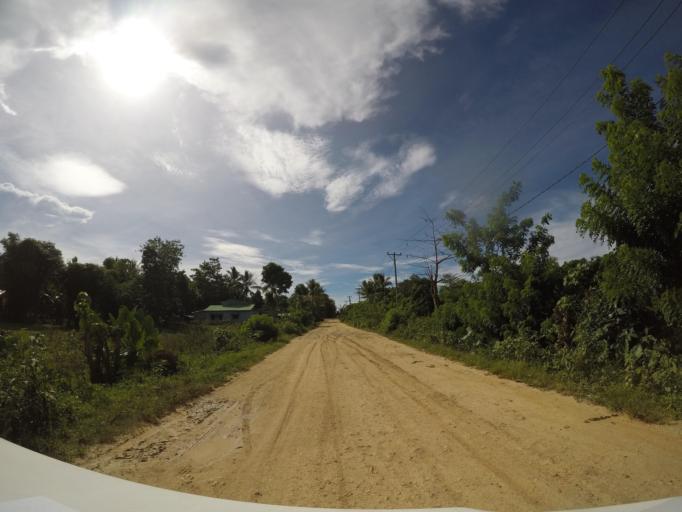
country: TL
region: Lautem
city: Lospalos
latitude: -8.4989
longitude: 126.9979
